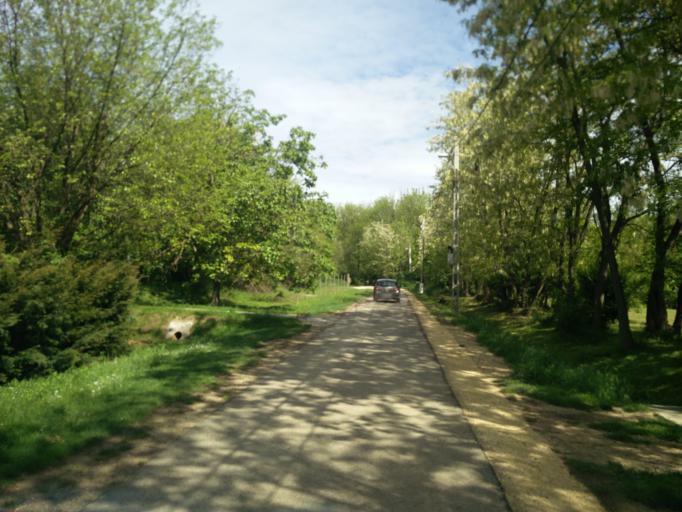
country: HU
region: Tolna
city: Szentgalpuszta
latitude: 46.2836
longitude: 18.6364
